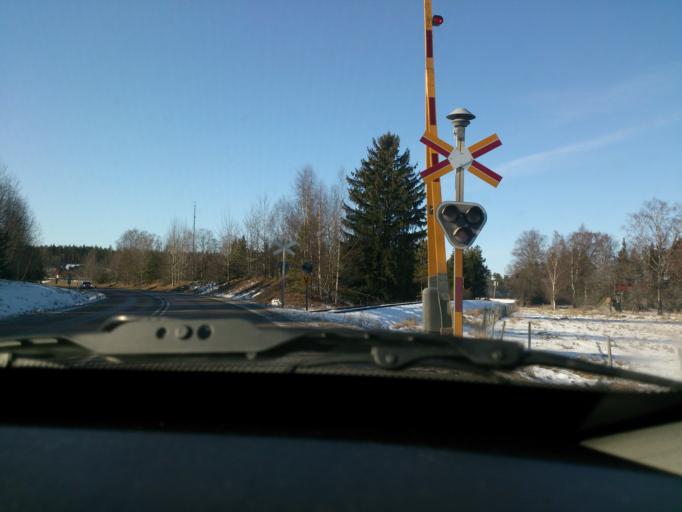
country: SE
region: Uppsala
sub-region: Uppsala Kommun
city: Saevja
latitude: 59.8579
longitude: 17.8118
